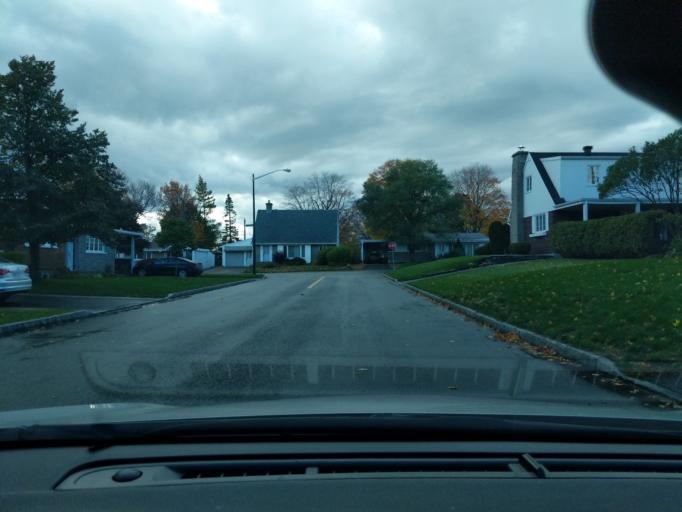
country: CA
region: Quebec
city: L'Ancienne-Lorette
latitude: 46.7628
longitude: -71.2908
